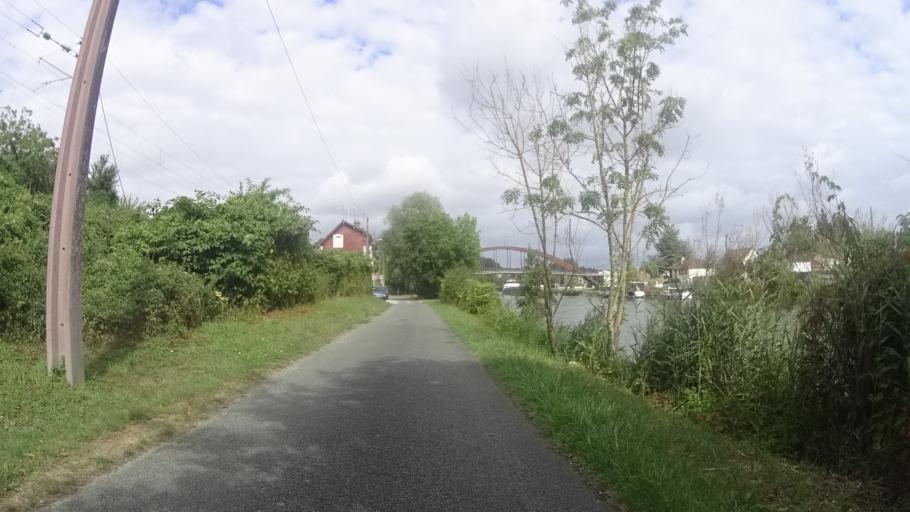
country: FR
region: Picardie
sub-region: Departement de l'Oise
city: Longueil-Annel
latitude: 49.4547
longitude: 2.8628
